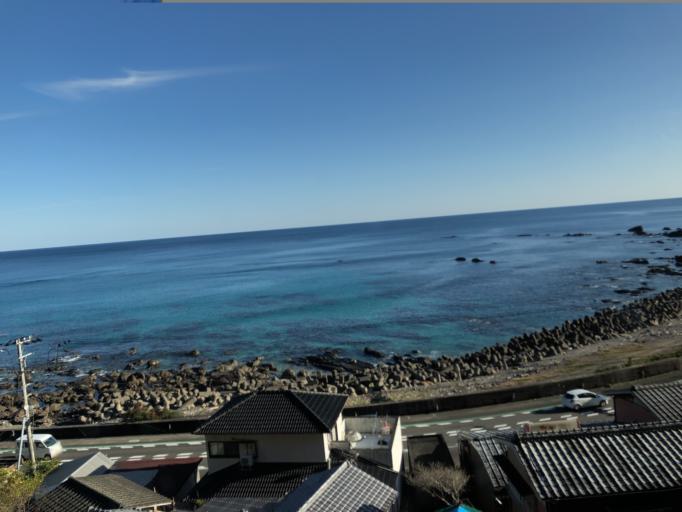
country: JP
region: Kochi
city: Nakamura
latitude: 33.0595
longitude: 133.0998
